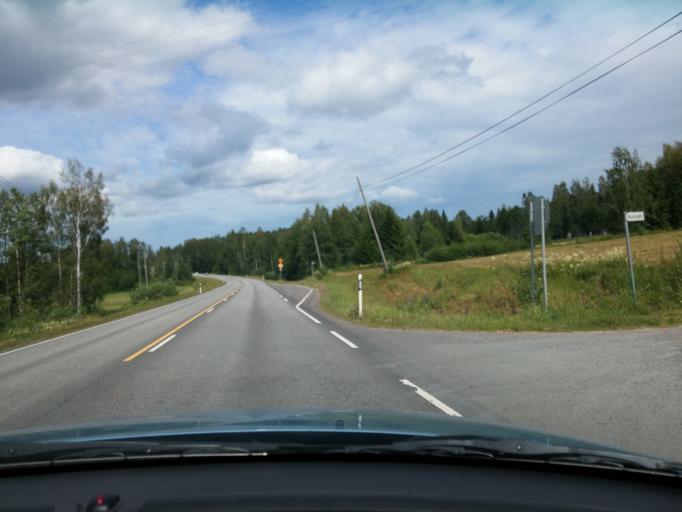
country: FI
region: Central Finland
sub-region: Saarijaervi-Viitasaari
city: Saarijaervi
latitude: 62.7278
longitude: 25.1948
